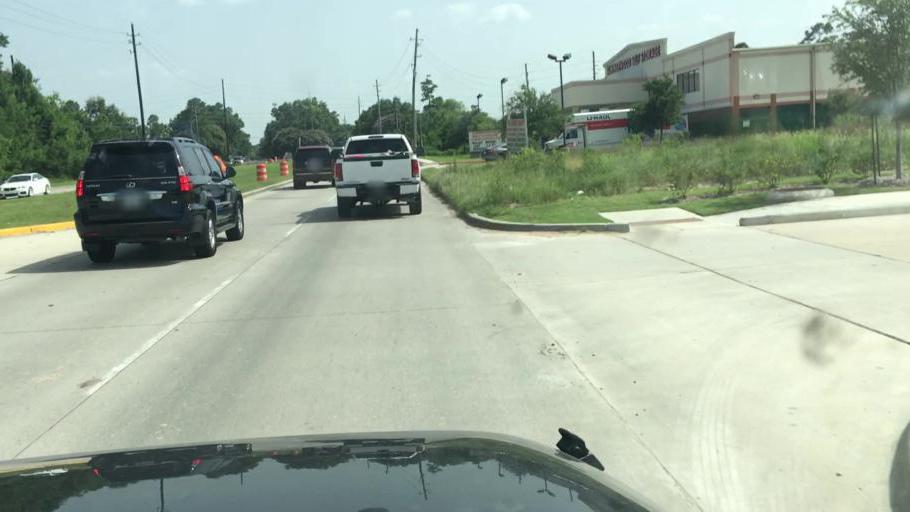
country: US
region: Texas
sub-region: Harris County
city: Atascocita
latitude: 29.9366
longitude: -95.1762
